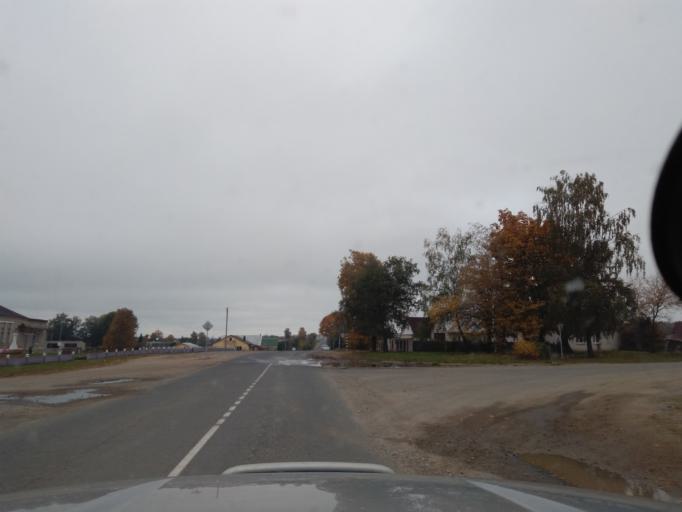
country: BY
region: Minsk
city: Kapyl'
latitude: 53.1510
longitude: 27.1424
